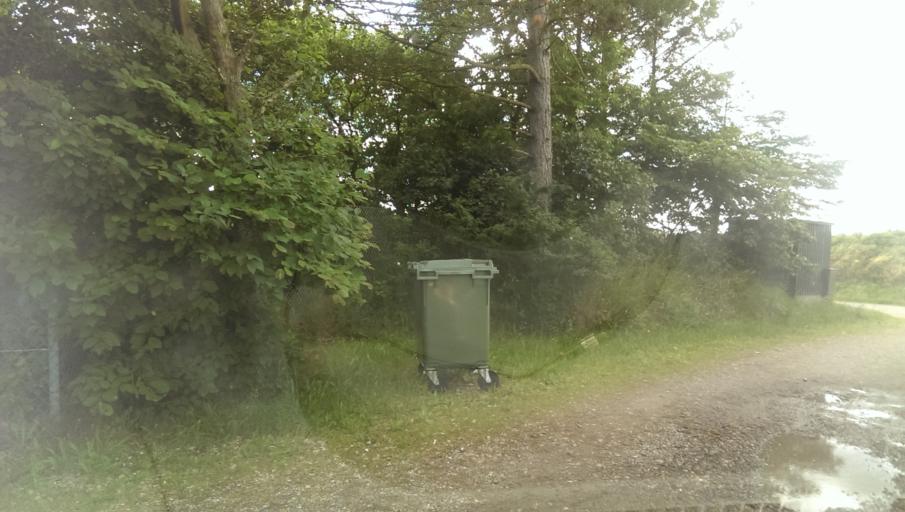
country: DK
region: Central Jutland
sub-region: Holstebro Kommune
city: Ulfborg
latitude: 56.2670
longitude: 8.2476
